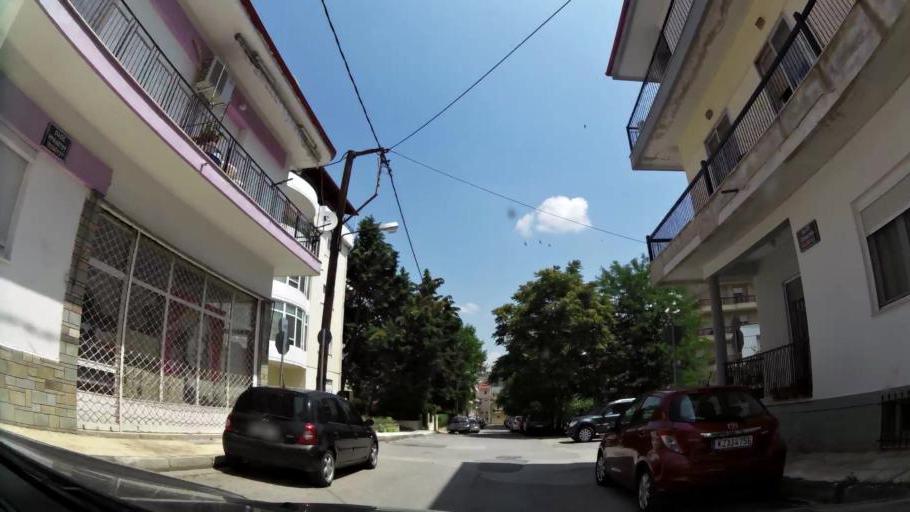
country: GR
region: West Macedonia
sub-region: Nomos Kozanis
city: Kozani
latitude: 40.2980
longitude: 21.7831
